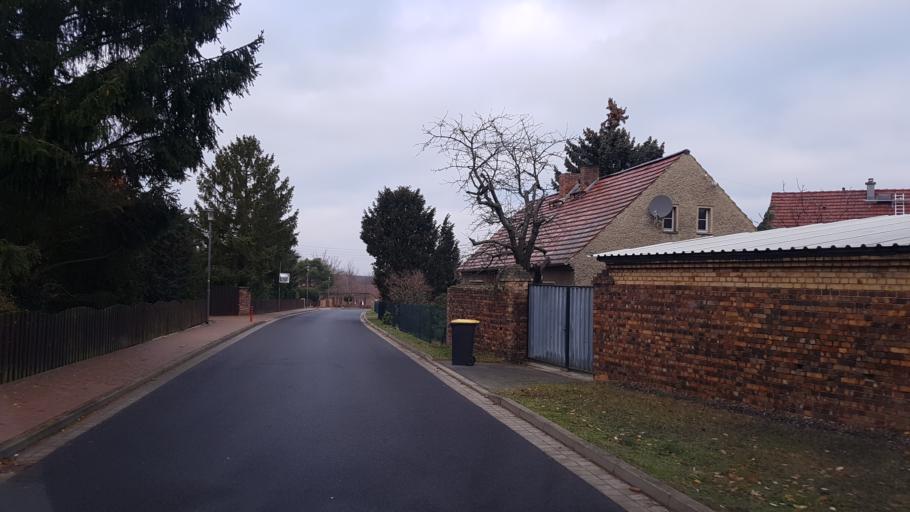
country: DE
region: Brandenburg
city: Sallgast
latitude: 51.5867
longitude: 13.8178
